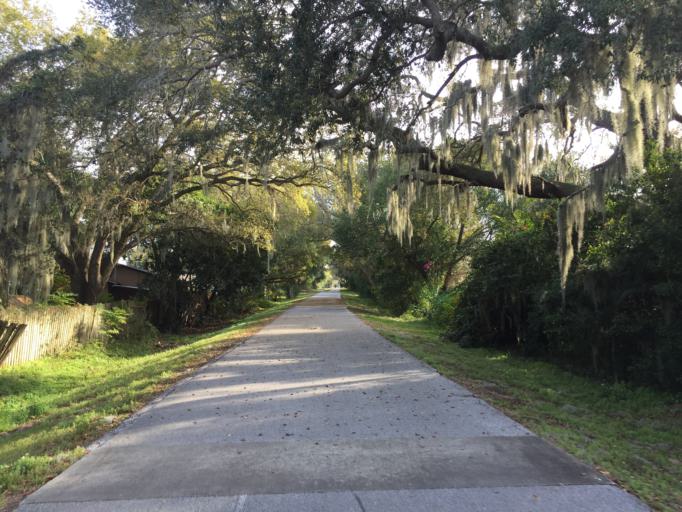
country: US
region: Florida
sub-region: Pinellas County
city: Dunedin
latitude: 27.9973
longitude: -82.7888
